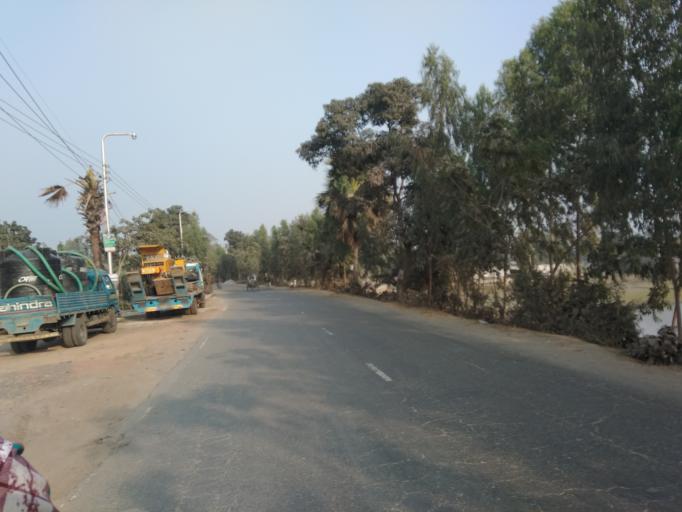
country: BD
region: Rajshahi
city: Par Naogaon
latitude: 24.5001
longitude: 89.1450
